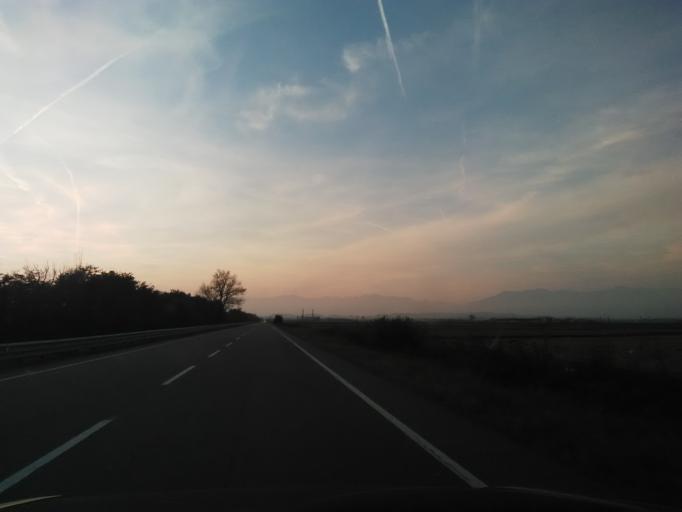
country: IT
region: Piedmont
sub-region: Provincia di Vercelli
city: Crova
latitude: 45.3555
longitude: 8.2191
